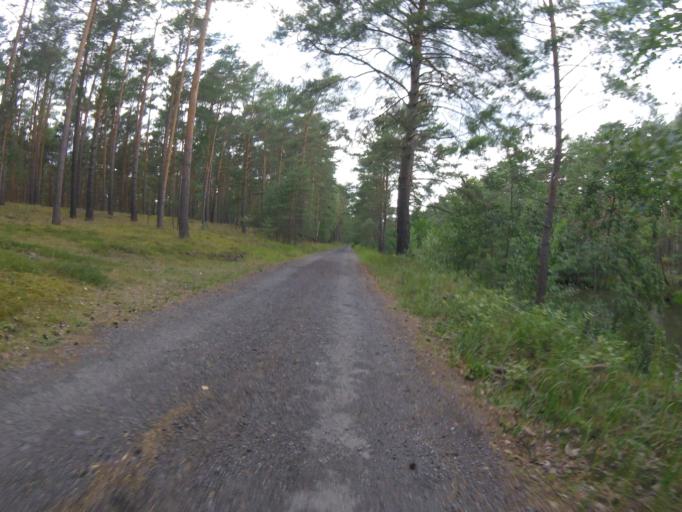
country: DE
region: Brandenburg
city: Munchehofe
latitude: 52.0957
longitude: 13.7900
